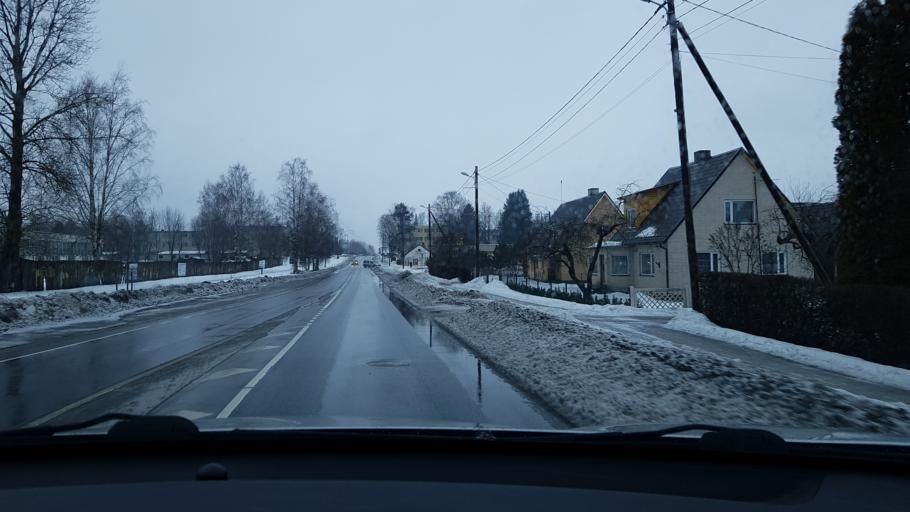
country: EE
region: Jaervamaa
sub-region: Tueri vald
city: Tueri
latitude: 58.8114
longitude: 25.4100
